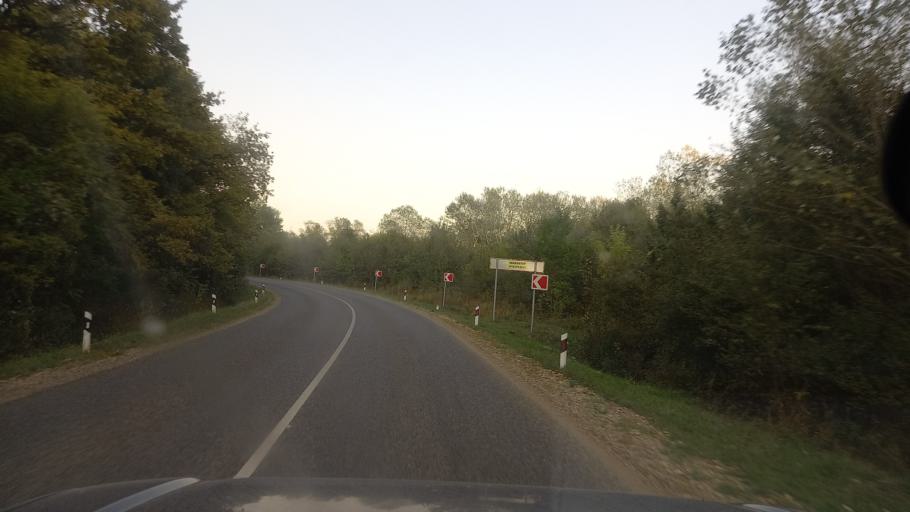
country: RU
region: Krasnodarskiy
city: Smolenskaya
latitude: 44.7500
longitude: 38.7617
